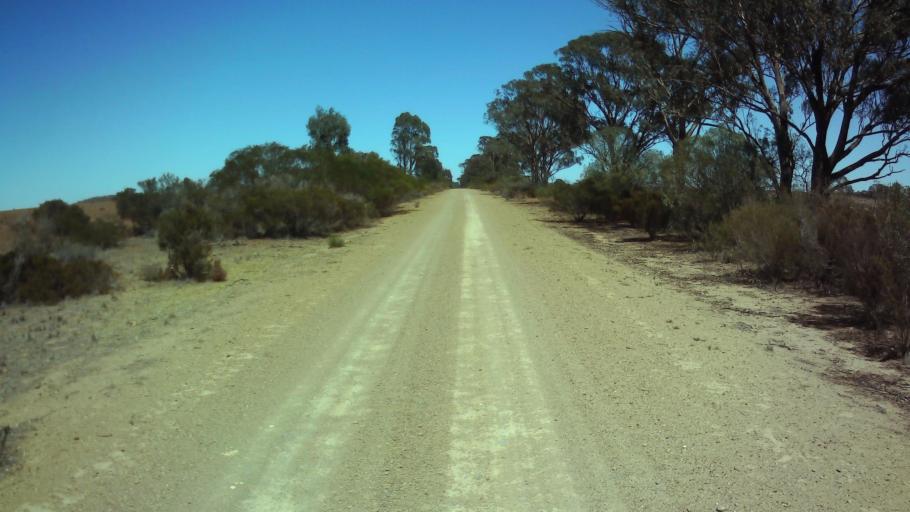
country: AU
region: New South Wales
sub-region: Forbes
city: Forbes
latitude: -33.6940
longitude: 147.8223
